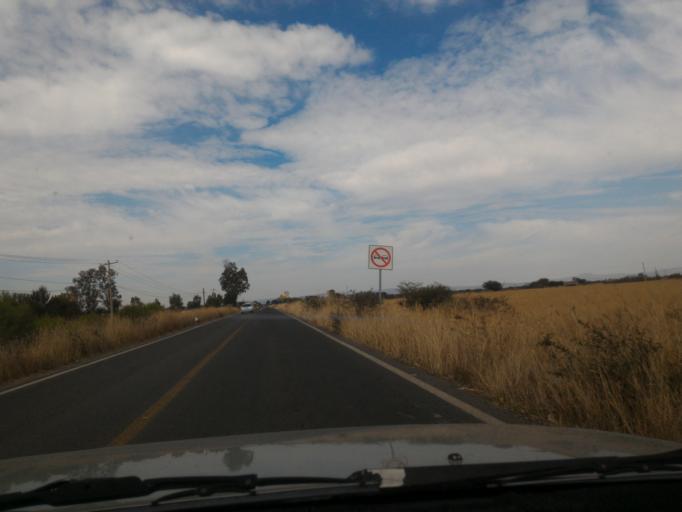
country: MX
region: Guanajuato
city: Ciudad Manuel Doblado
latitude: 20.7590
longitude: -101.9667
